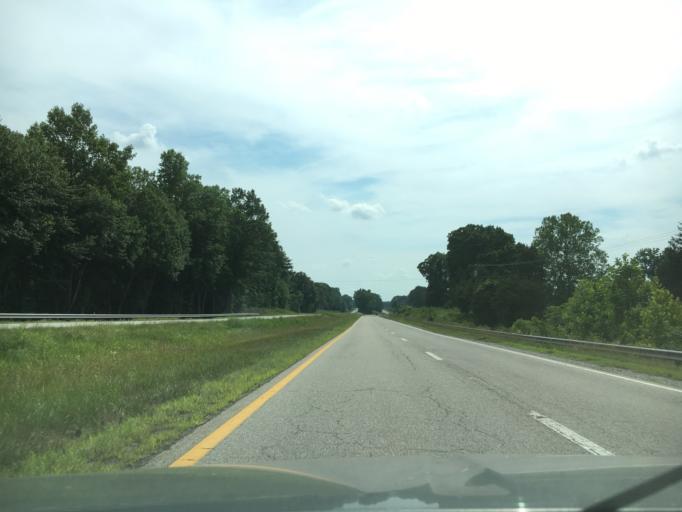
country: US
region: Virginia
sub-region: Nottoway County
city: Crewe
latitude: 37.1503
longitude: -78.2862
